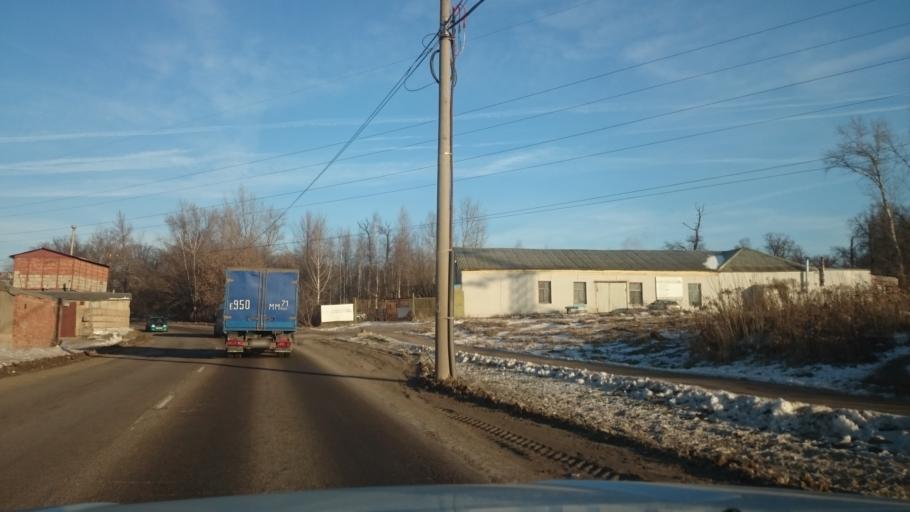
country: RU
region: Tula
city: Tula
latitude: 54.2183
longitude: 37.6854
